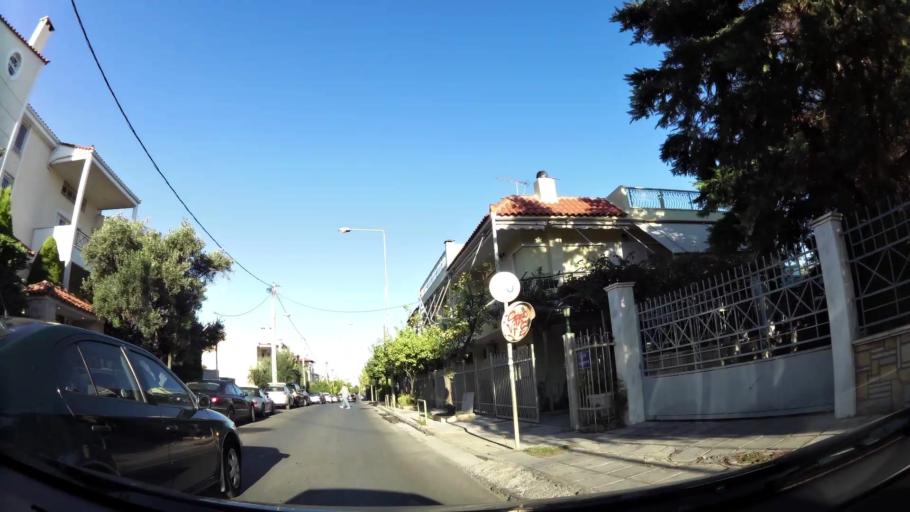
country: GR
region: Attica
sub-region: Nomarchia Athinas
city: Vrilissia
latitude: 38.0279
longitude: 23.8413
